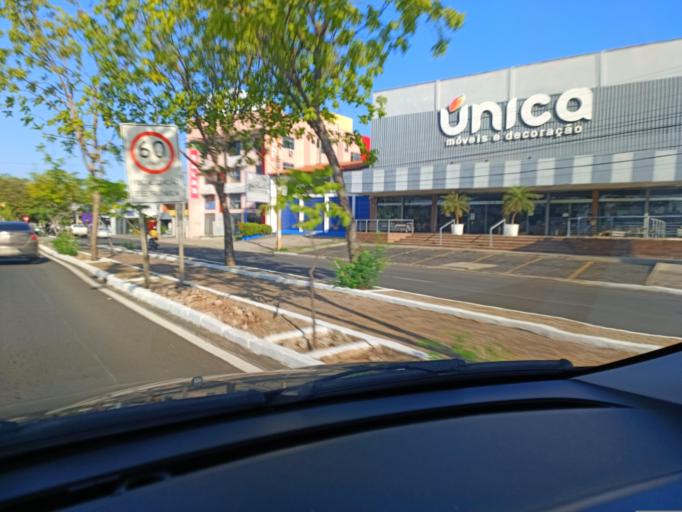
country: BR
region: Piaui
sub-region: Teresina
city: Teresina
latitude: -5.0804
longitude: -42.7840
